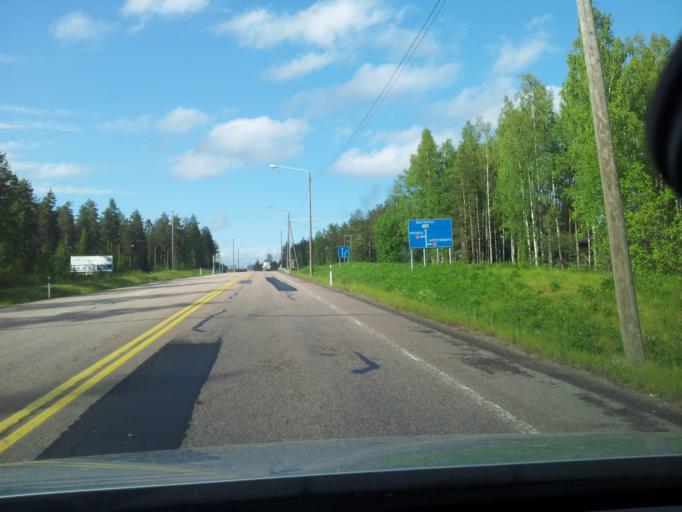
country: FI
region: South Karelia
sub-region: Lappeenranta
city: Luumaeki
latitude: 60.9248
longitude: 27.5815
